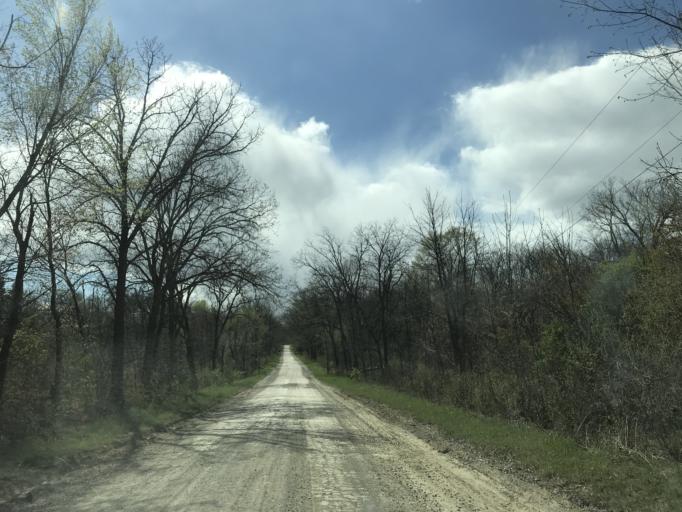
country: US
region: Michigan
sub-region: Livingston County
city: Whitmore Lake
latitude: 42.4034
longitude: -83.7048
